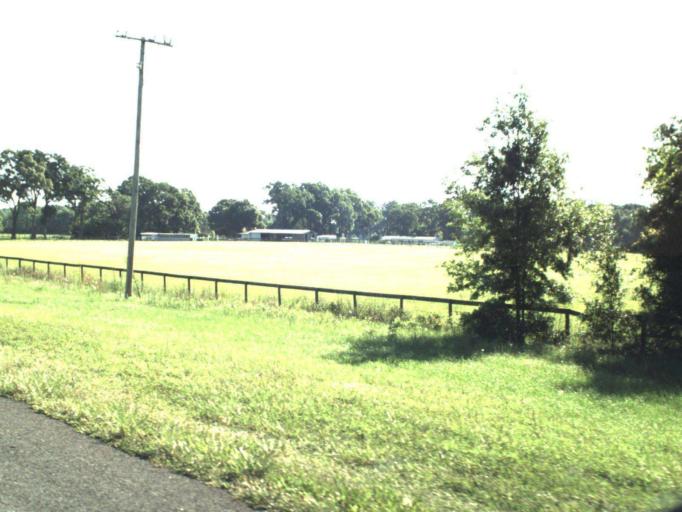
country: US
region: Florida
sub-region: Marion County
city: Citra
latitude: 29.3547
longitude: -82.1426
